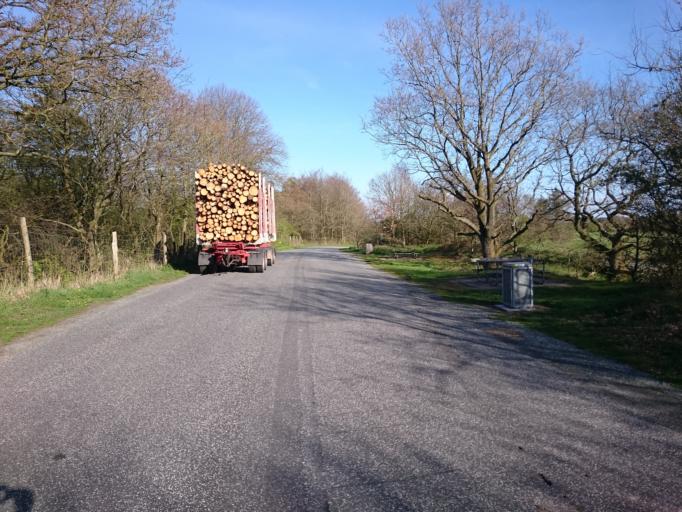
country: DK
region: South Denmark
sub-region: Haderslev Kommune
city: Gram
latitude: 55.2869
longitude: 8.9572
